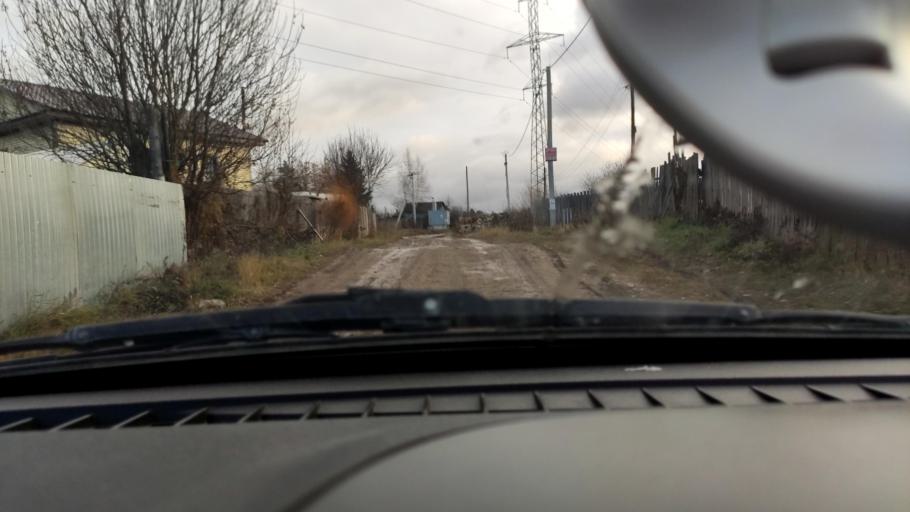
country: RU
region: Perm
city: Kondratovo
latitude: 57.9561
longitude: 56.1464
